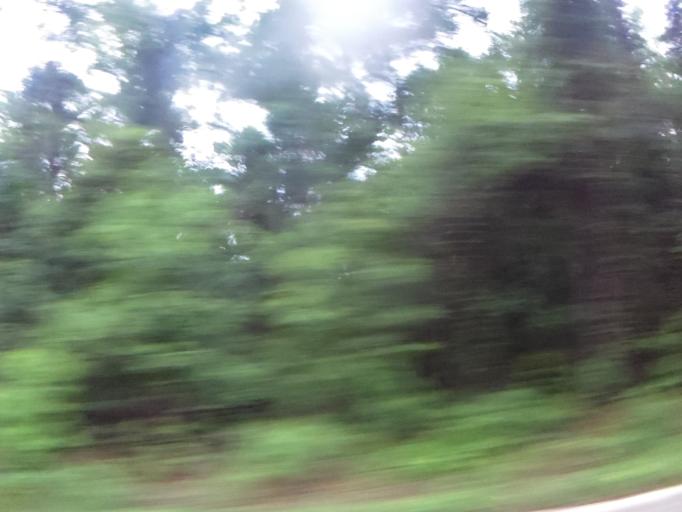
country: US
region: Florida
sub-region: Duval County
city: Jacksonville
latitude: 30.2779
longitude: -81.5647
